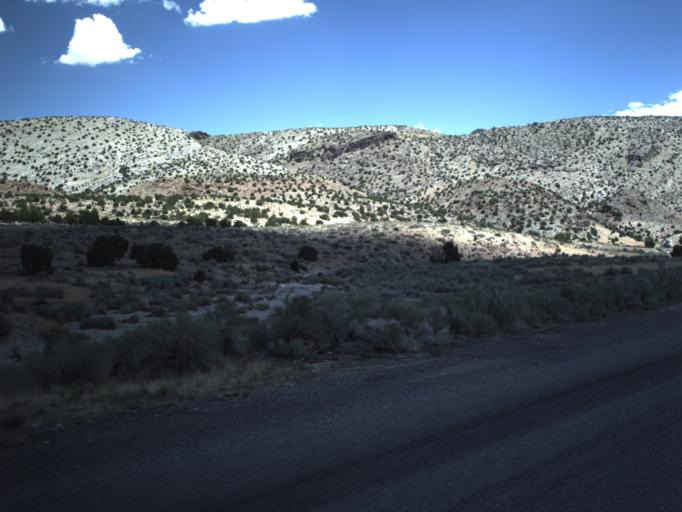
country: US
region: Utah
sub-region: Beaver County
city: Milford
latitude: 39.0790
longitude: -113.6093
